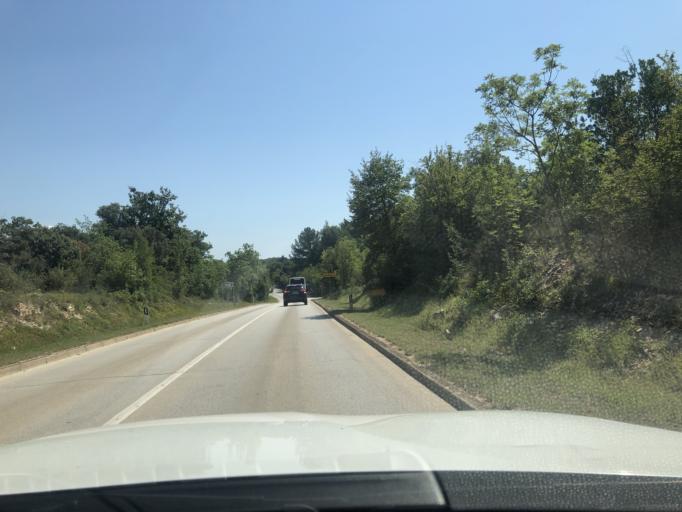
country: HR
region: Istarska
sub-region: Grad Rovinj
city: Rovinj
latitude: 45.0530
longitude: 13.7155
